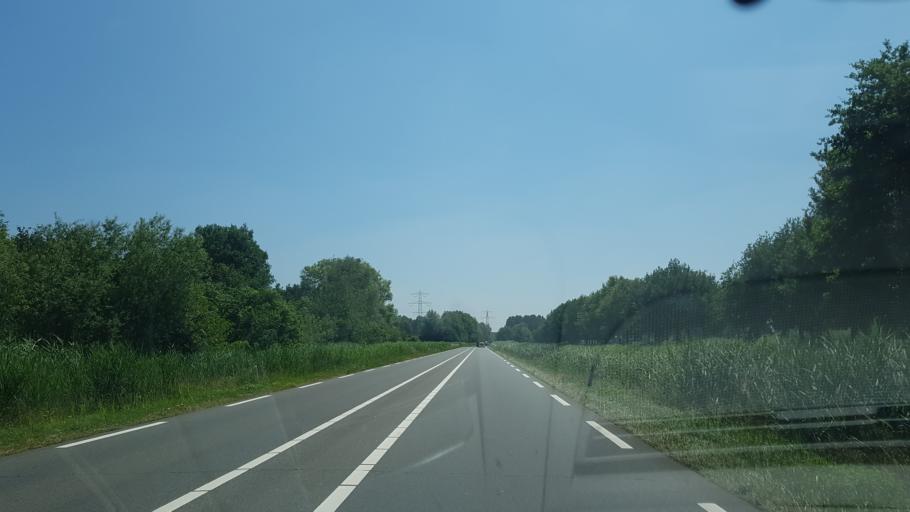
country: NL
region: North Brabant
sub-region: Gemeente Helmond
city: Helmond
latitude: 51.5040
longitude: 5.6723
